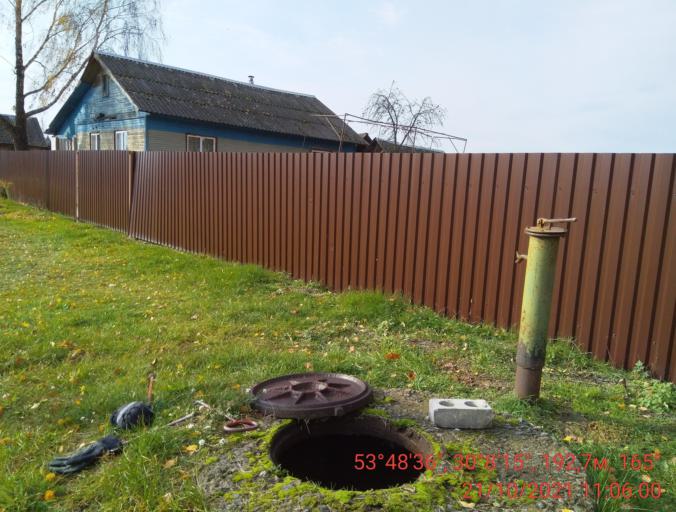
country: BY
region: Mogilev
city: Myazhysyatki
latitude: 53.8101
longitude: 30.1376
